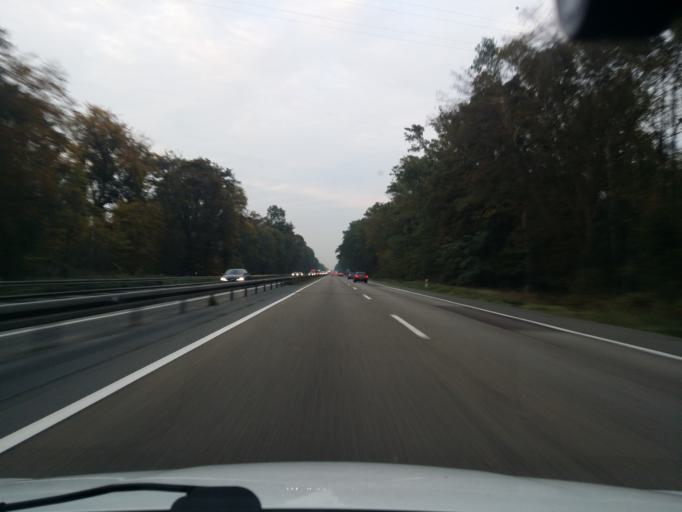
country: DE
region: Hesse
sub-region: Regierungsbezirk Darmstadt
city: Einhausen
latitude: 49.6889
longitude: 8.5517
